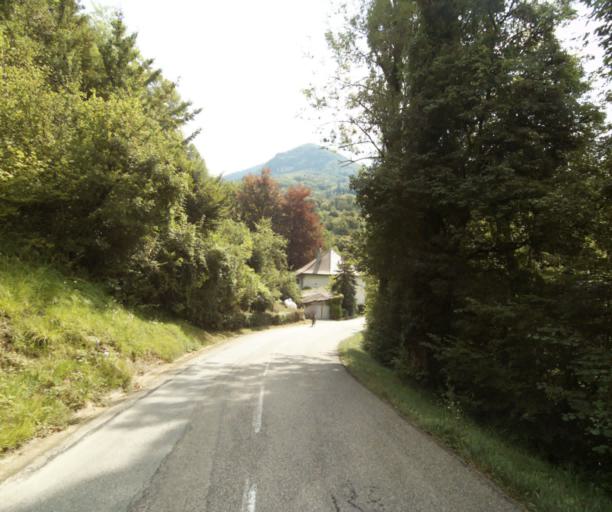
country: FR
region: Rhone-Alpes
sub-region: Departement de l'Isere
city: Saint-Egreve
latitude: 45.2501
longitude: 5.7236
